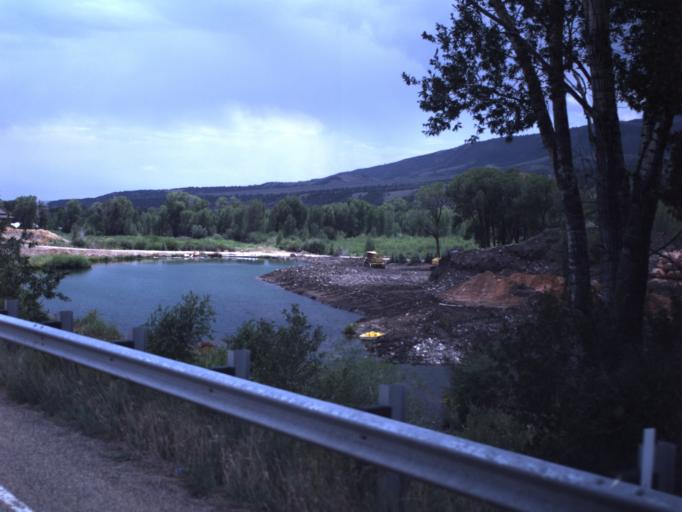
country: US
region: Utah
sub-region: Duchesne County
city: Duchesne
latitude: 40.4196
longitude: -110.7913
